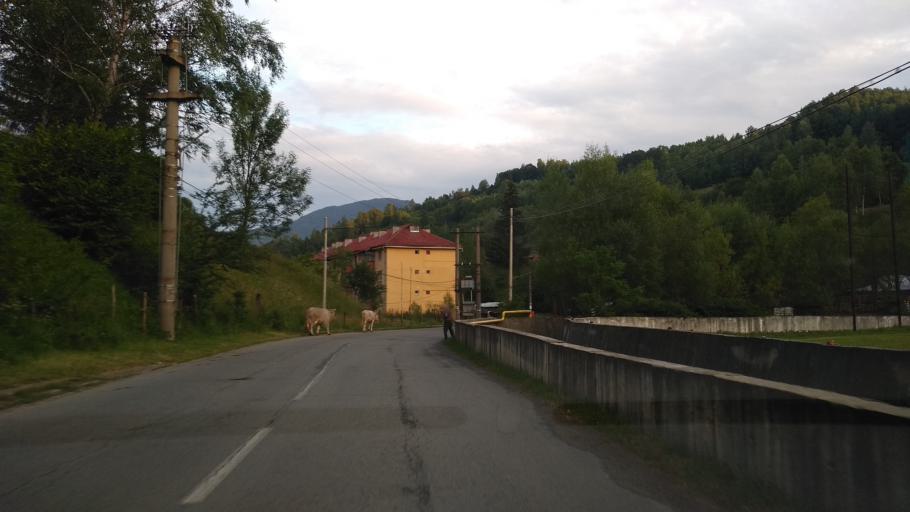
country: RO
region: Hunedoara
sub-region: Comuna Aninoasa
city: Aninoasa
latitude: 45.3923
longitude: 23.3185
